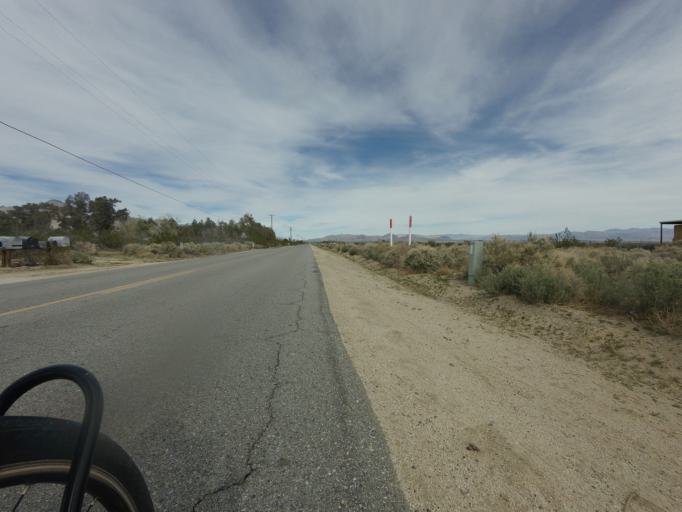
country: US
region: California
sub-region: Kern County
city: Inyokern
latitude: 35.7471
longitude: -117.8421
